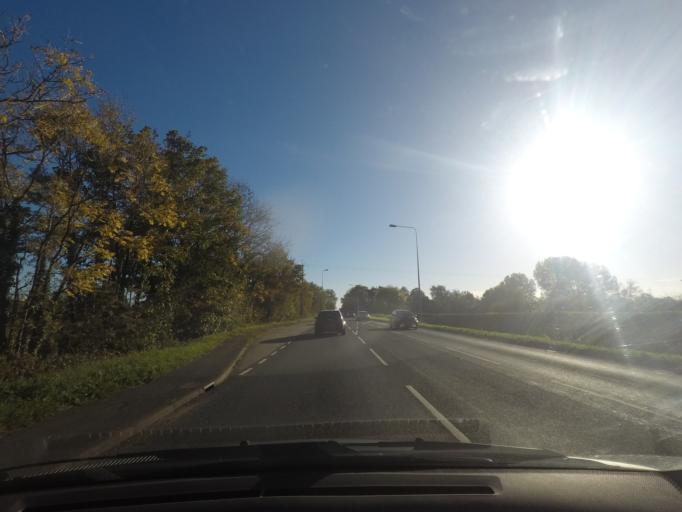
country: GB
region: England
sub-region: City of York
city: Holtby
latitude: 53.9547
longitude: -0.9710
